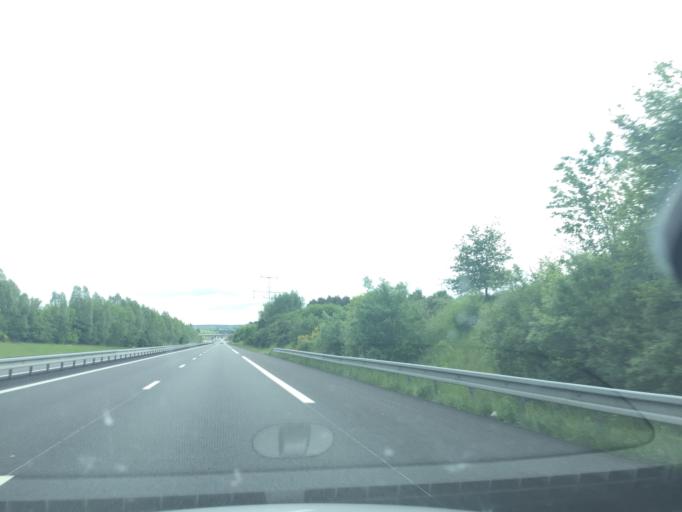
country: FR
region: Pays de la Loire
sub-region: Departement de la Sarthe
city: Ecommoy
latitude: 47.8291
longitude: 0.3063
